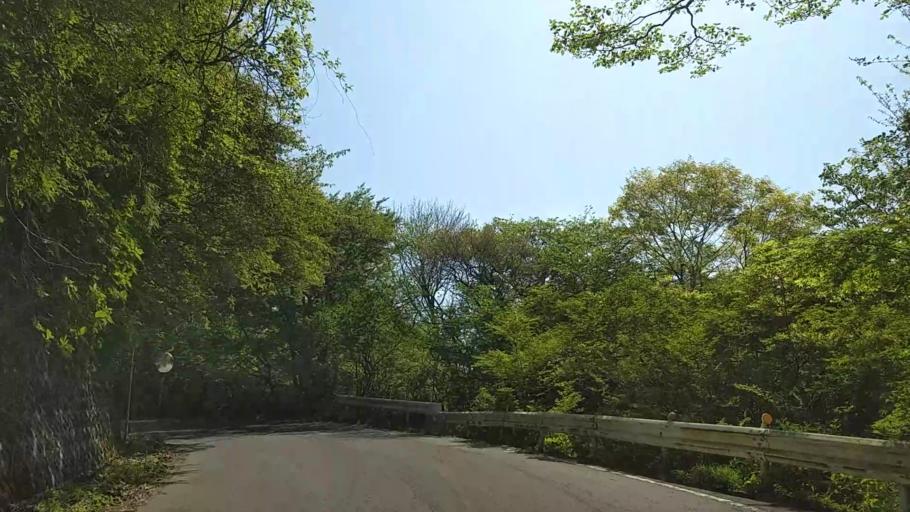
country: JP
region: Shizuoka
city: Gotemba
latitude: 35.2669
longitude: 138.9644
